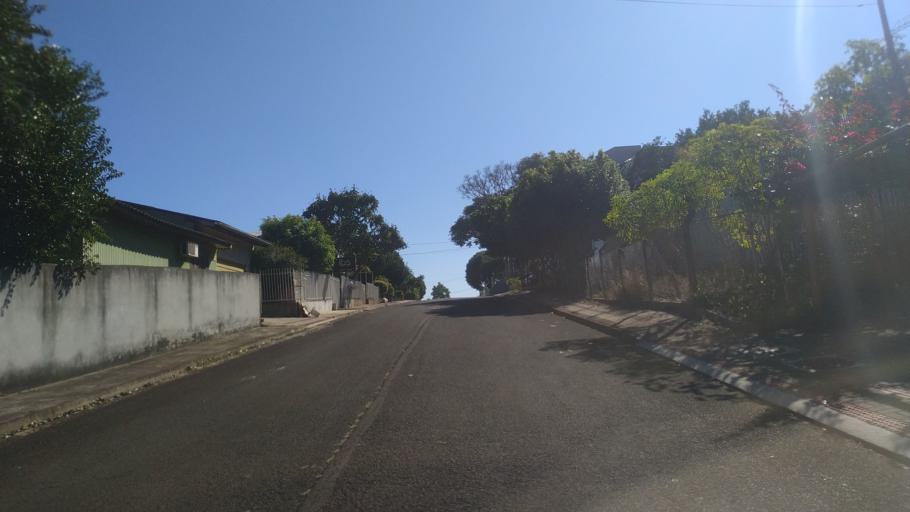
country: BR
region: Santa Catarina
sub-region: Chapeco
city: Chapeco
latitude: -27.1121
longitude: -52.6011
